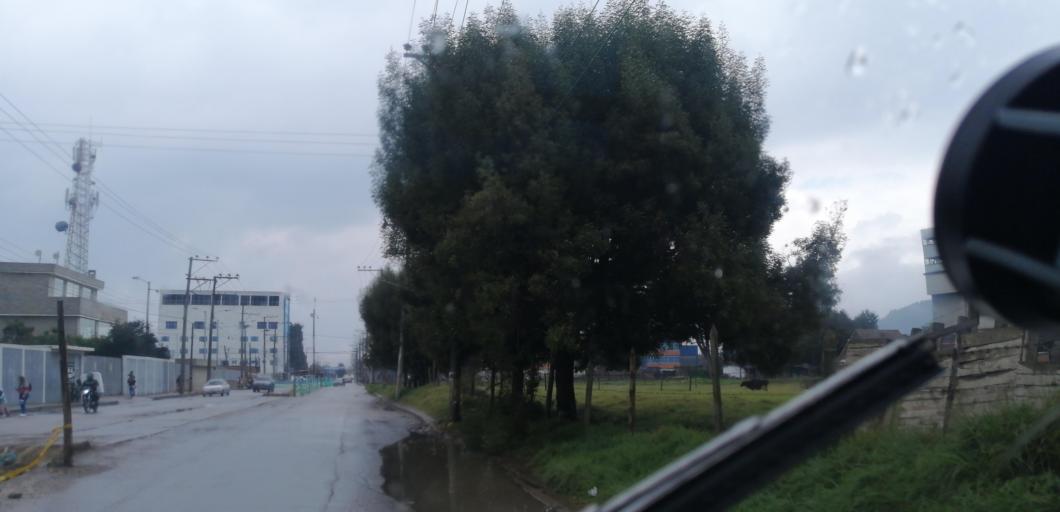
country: CO
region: Cundinamarca
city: Madrid
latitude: 4.7338
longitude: -74.2560
